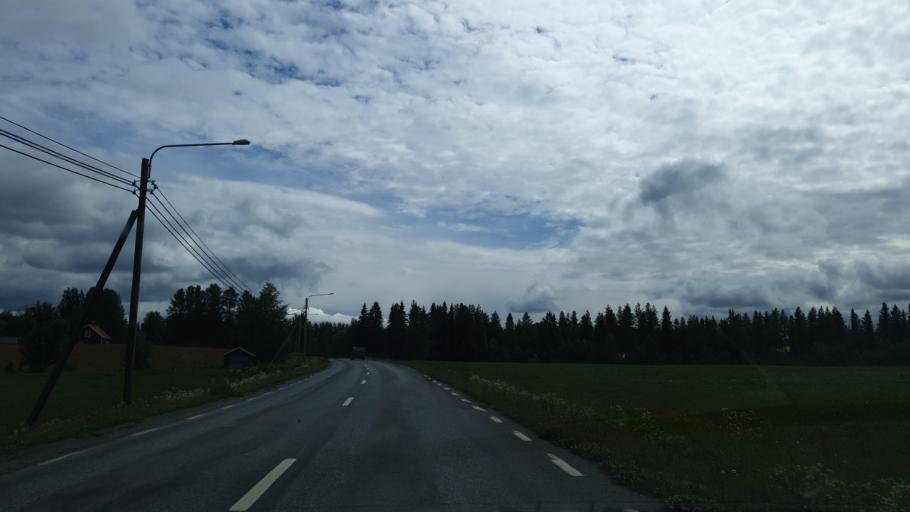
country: SE
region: Vaesterbotten
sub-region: Vilhelmina Kommun
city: Sjoberg
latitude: 64.6417
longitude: 16.3568
